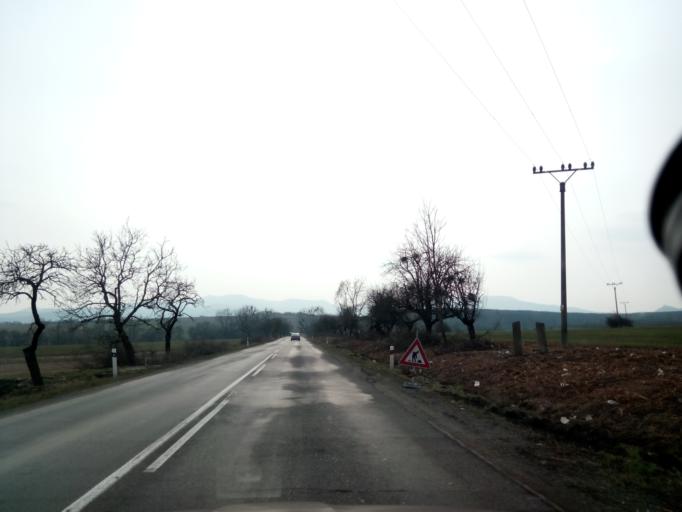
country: SK
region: Kosicky
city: Secovce
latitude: 48.6417
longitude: 21.5641
